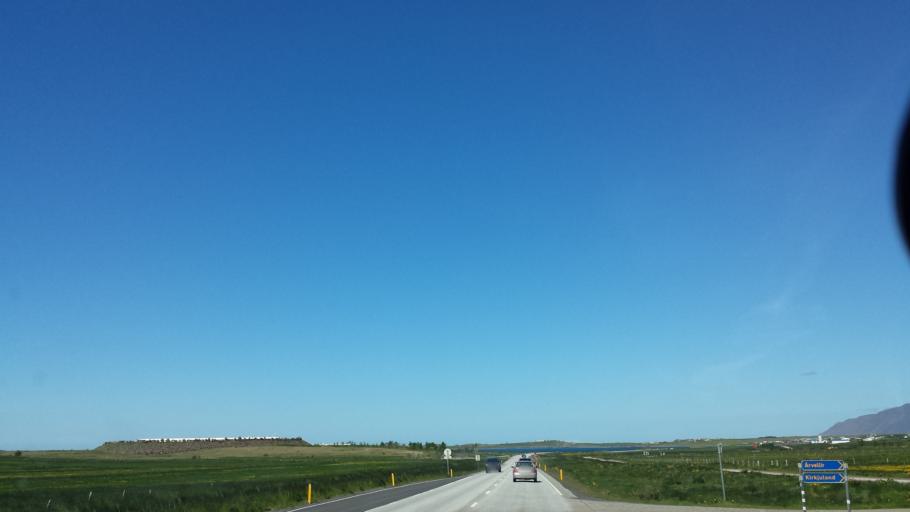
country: IS
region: Capital Region
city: Mosfellsbaer
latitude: 64.2172
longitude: -21.7899
